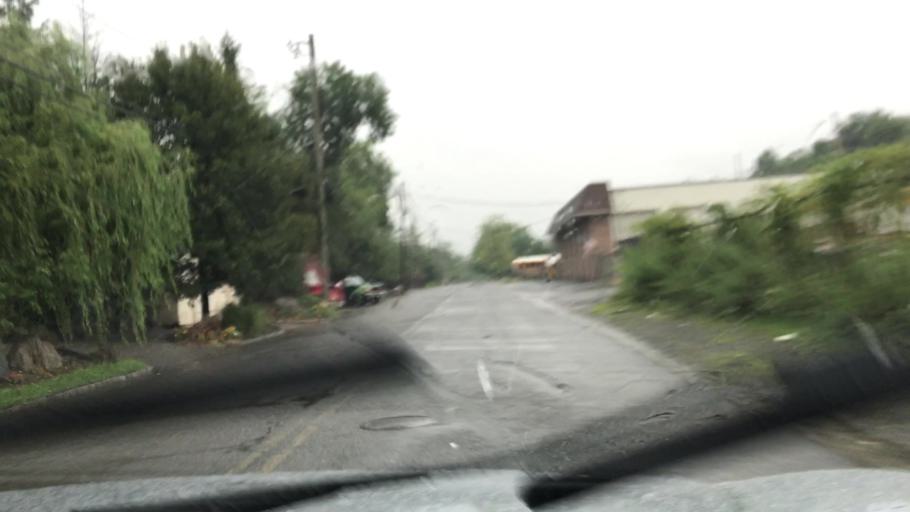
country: US
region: New Jersey
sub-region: Bergen County
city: Closter
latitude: 40.9768
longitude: -73.9609
